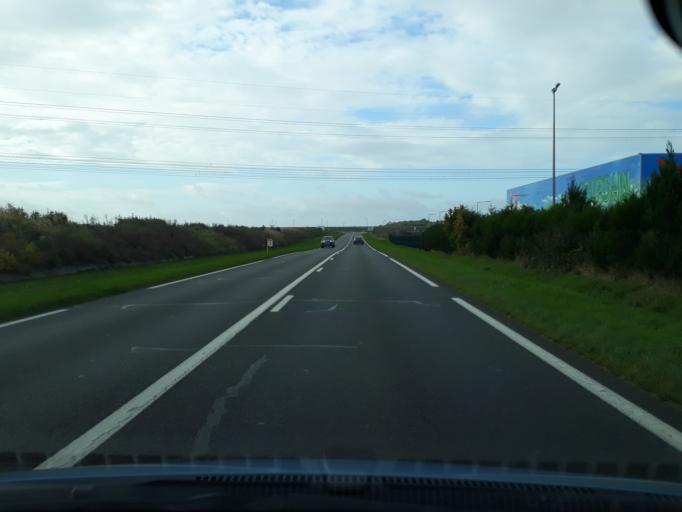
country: FR
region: Centre
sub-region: Departement du Loiret
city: Pithiviers-le-Vieil
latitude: 48.1228
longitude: 2.1906
